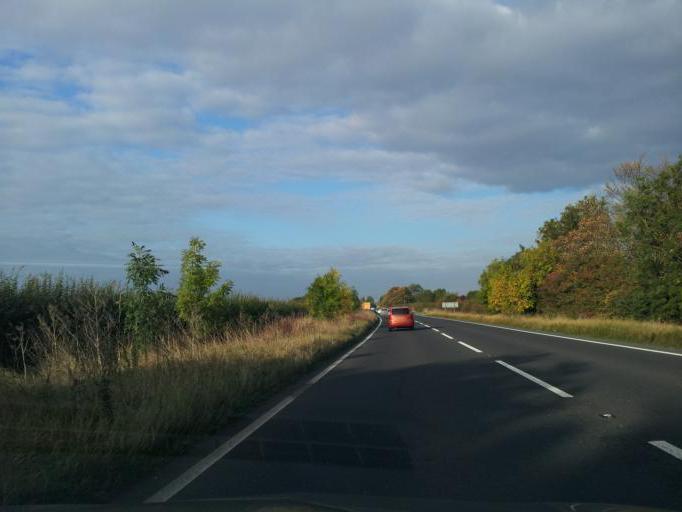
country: GB
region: England
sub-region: Nottinghamshire
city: Bingham
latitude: 52.9450
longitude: -0.9011
